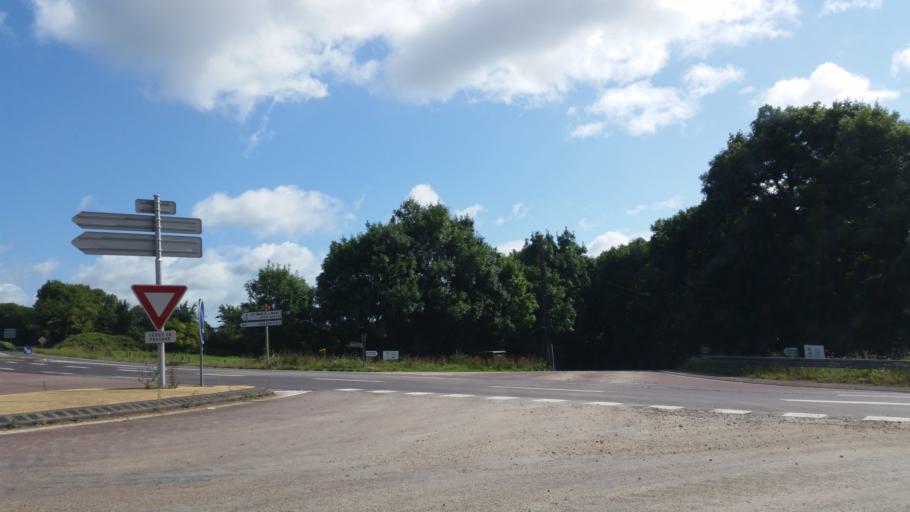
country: FR
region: Lower Normandy
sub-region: Departement de la Manche
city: Carentan
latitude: 49.3281
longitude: -1.2687
